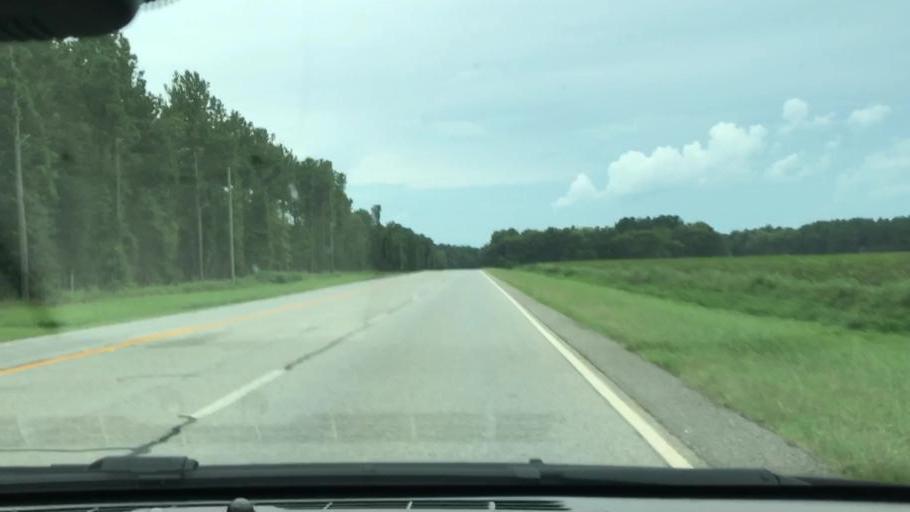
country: US
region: Georgia
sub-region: Early County
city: Blakely
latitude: 31.3372
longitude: -84.9885
